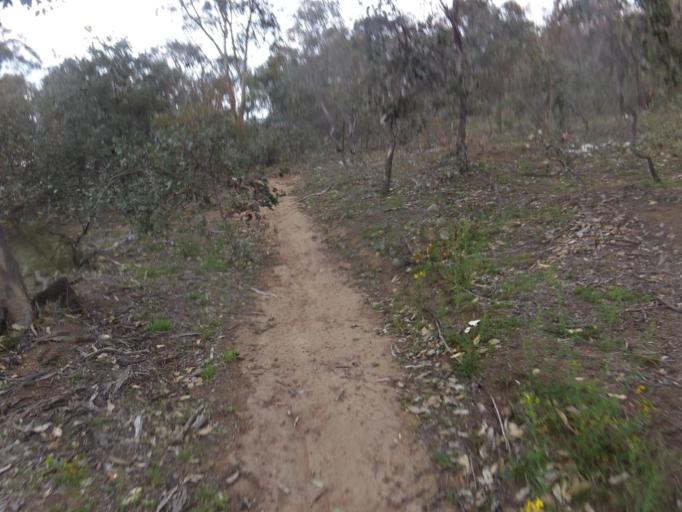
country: AU
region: Australian Capital Territory
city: Forrest
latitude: -35.3471
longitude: 149.1281
